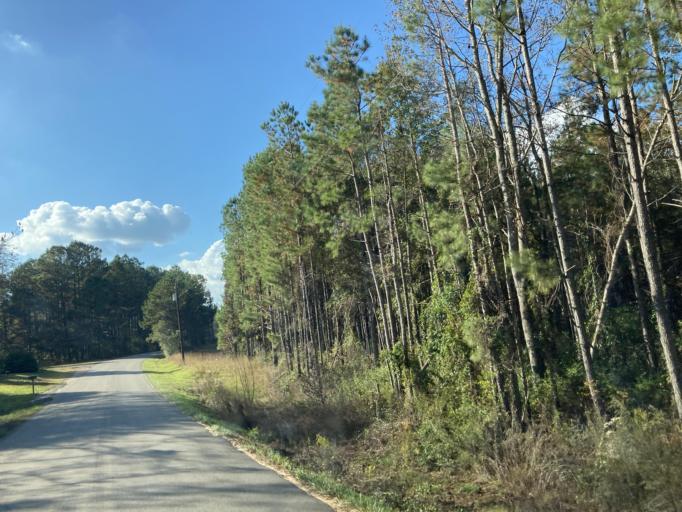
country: US
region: Mississippi
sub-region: Lamar County
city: Sumrall
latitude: 31.4268
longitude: -89.6431
